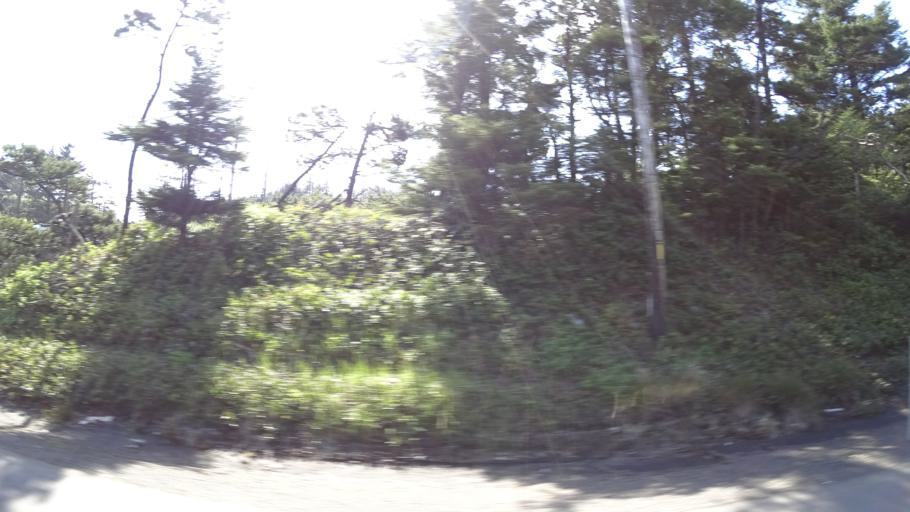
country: US
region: Oregon
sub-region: Lincoln County
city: Newport
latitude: 44.6779
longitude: -124.0615
